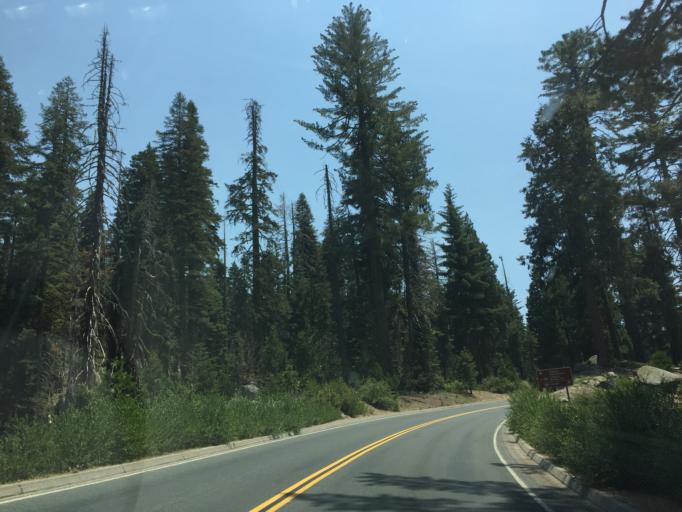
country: US
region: California
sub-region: Tulare County
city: Three Rivers
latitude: 36.7262
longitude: -118.9552
